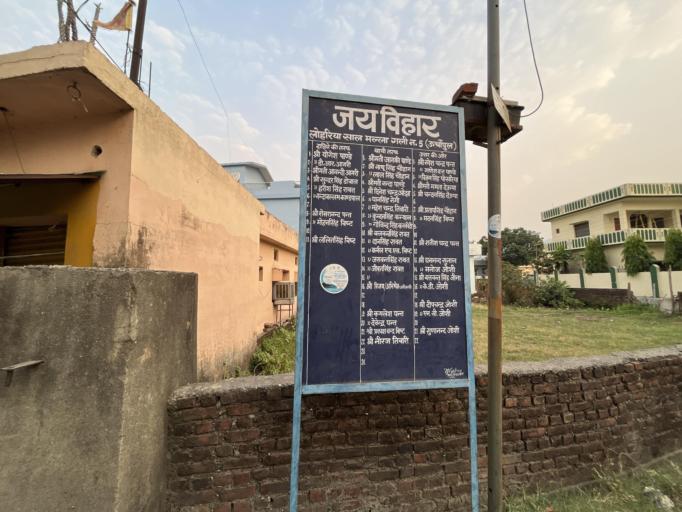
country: IN
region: Uttarakhand
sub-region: Naini Tal
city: Haldwani
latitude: 29.2273
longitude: 79.5002
